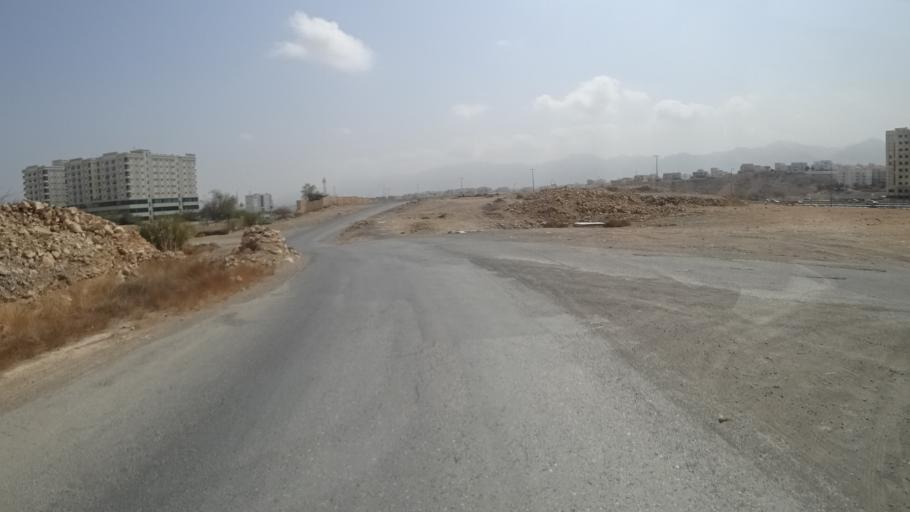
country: OM
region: Muhafazat Masqat
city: Bawshar
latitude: 23.5642
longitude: 58.3437
